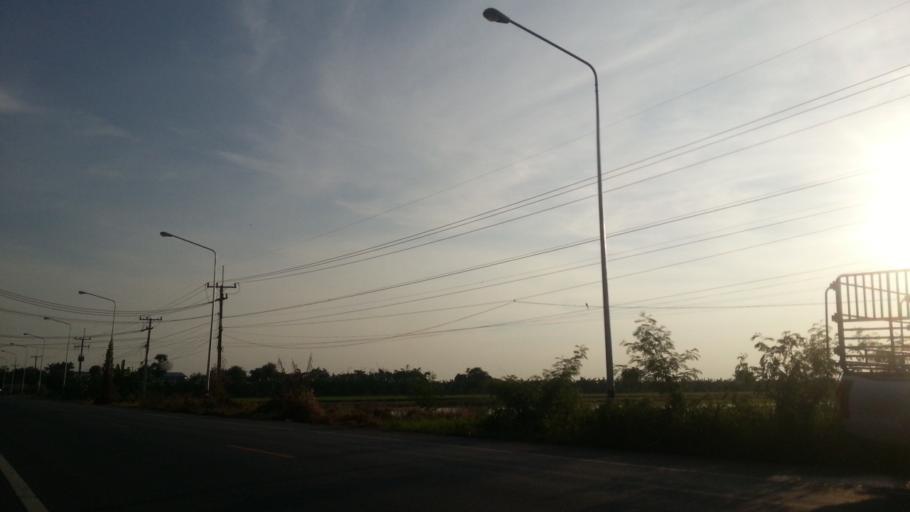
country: TH
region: Pathum Thani
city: Ban Rangsit
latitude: 14.0362
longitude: 100.8440
